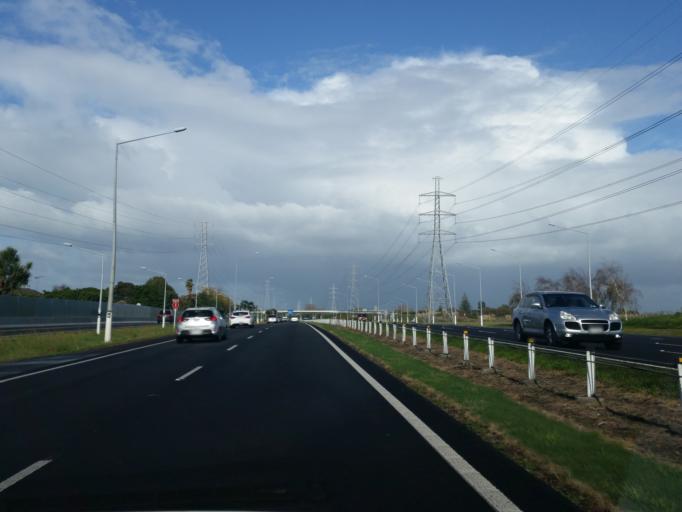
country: NZ
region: Auckland
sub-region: Auckland
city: Papakura
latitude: -37.0684
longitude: 174.9270
